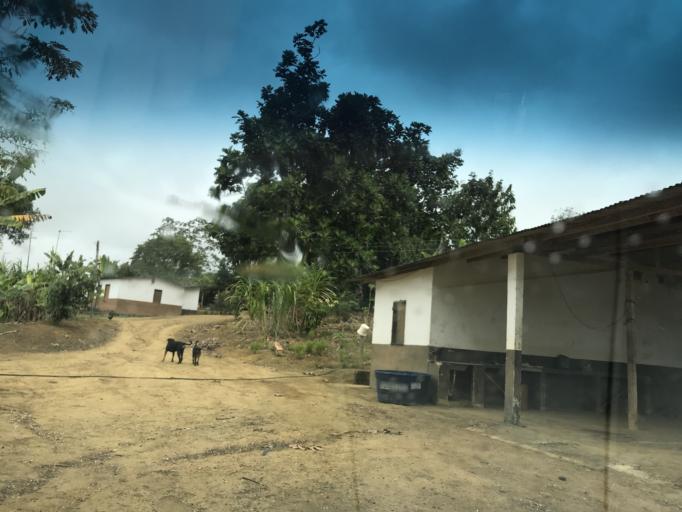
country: BR
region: Bahia
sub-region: Ibirapitanga
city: Ibirapitanga
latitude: -14.0480
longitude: -39.3558
